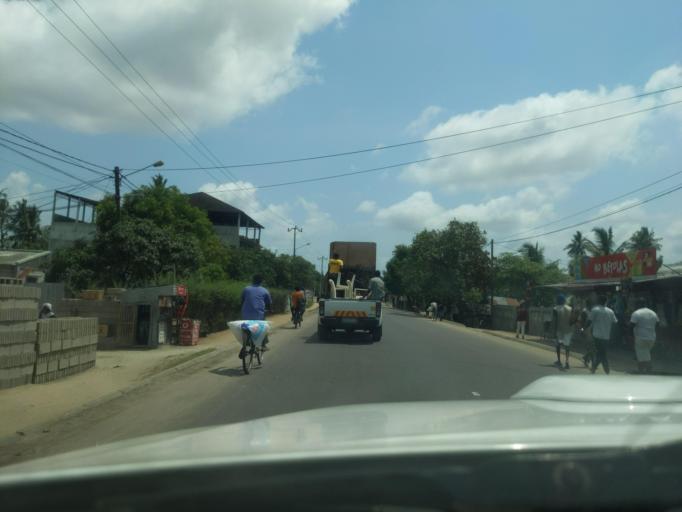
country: MZ
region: Zambezia
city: Quelimane
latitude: -17.8515
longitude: 36.9050
